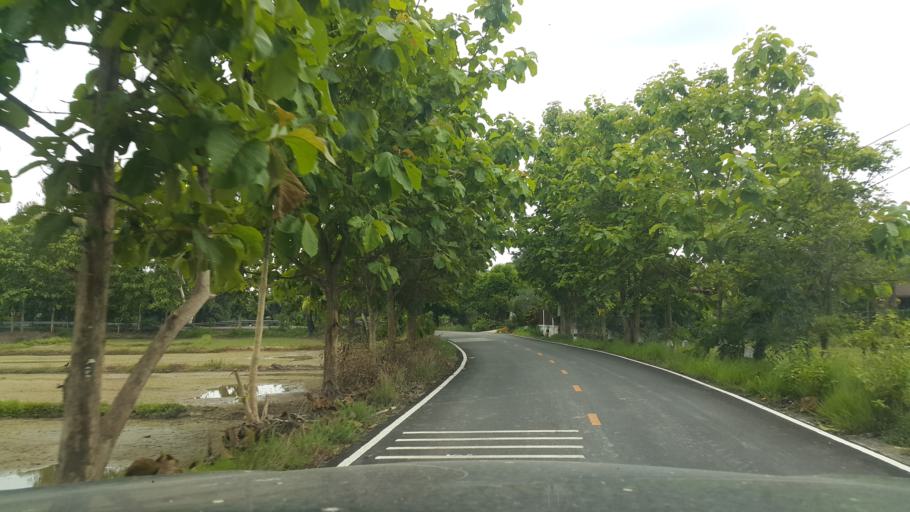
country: TH
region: Lamphun
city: Ban Thi
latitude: 18.6608
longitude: 99.1542
